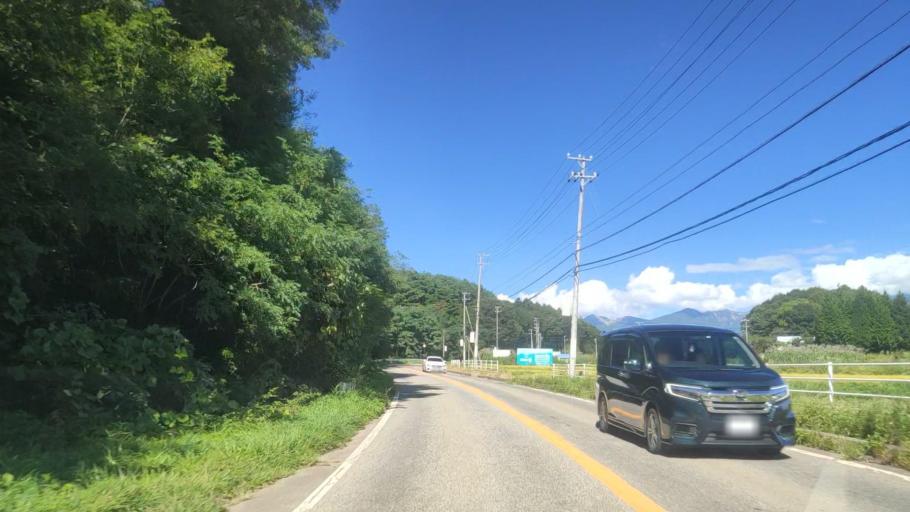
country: JP
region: Nagano
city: Chino
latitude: 35.9379
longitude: 138.2188
